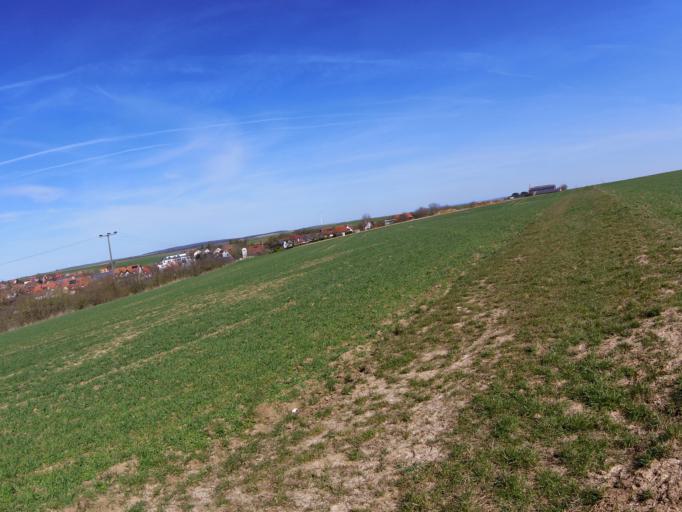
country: DE
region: Bavaria
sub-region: Regierungsbezirk Unterfranken
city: Biebelried
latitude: 49.7925
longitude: 10.1060
